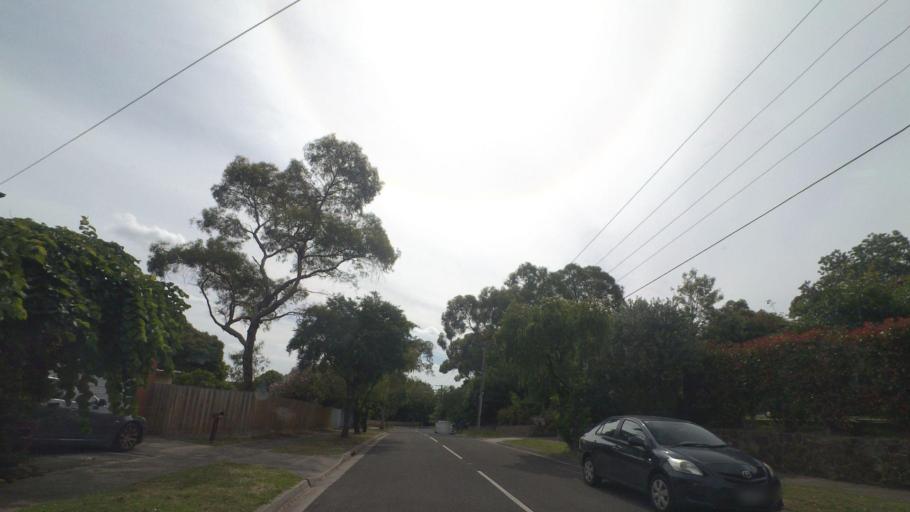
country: AU
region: Victoria
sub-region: Maroondah
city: Bayswater North
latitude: -37.8412
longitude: 145.2924
